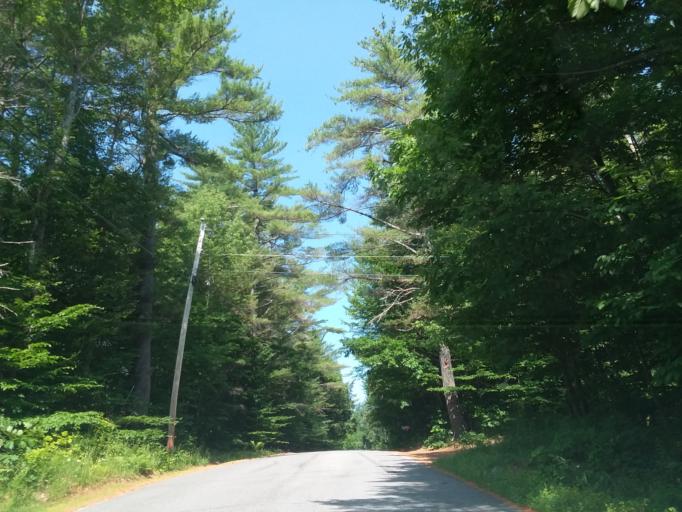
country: US
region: Maine
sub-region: Kennebec County
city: Monmouth
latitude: 44.2797
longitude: -70.0157
